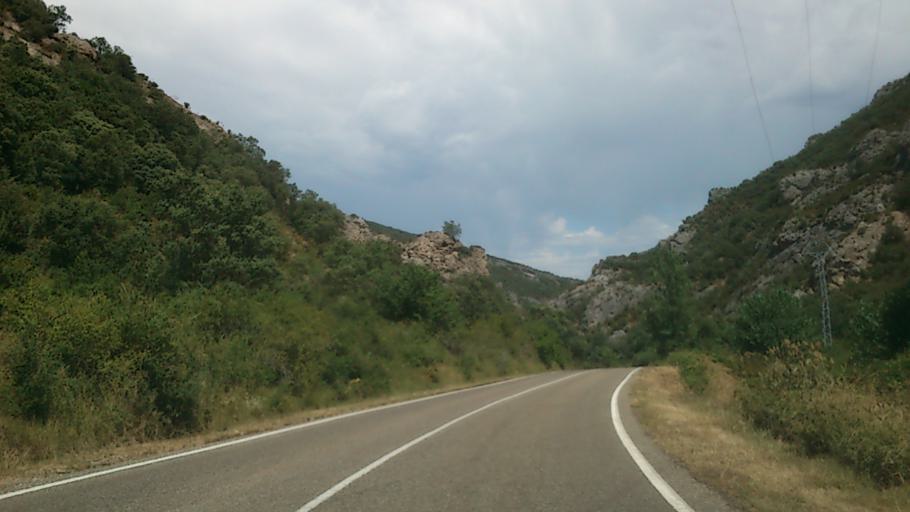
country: ES
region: Castille and Leon
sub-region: Provincia de Burgos
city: Frias
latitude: 42.7387
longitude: -3.3144
